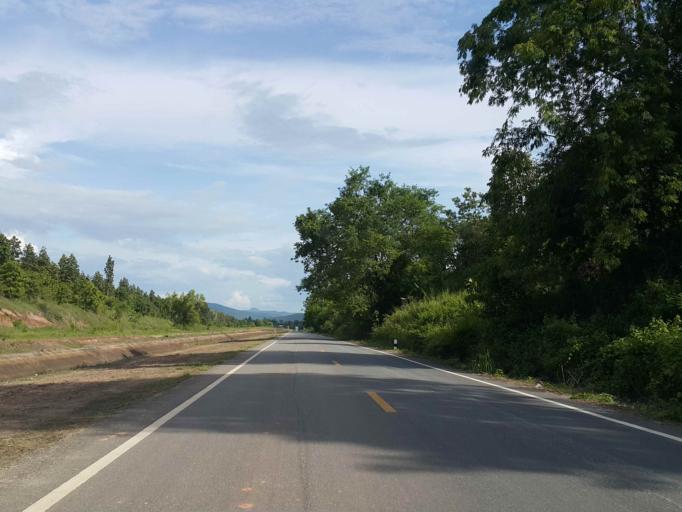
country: TH
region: Chiang Mai
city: San Sai
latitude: 18.8962
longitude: 99.1491
